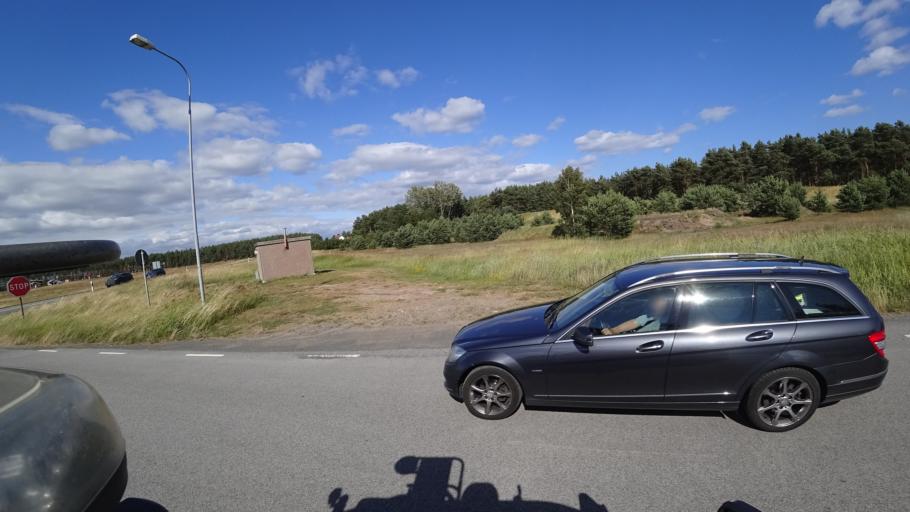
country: SE
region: Skane
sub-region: Kristianstads Kommun
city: Ahus
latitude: 55.8868
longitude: 14.2358
